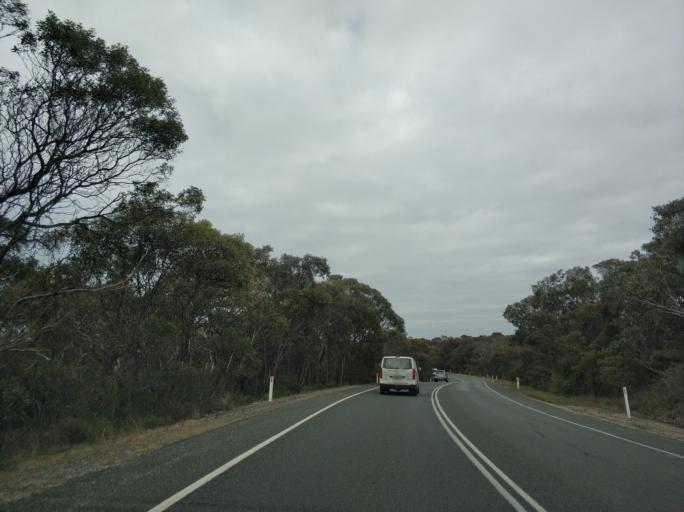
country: AU
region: Victoria
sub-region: Surf Coast
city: Anglesea
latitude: -38.4464
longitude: 144.1168
